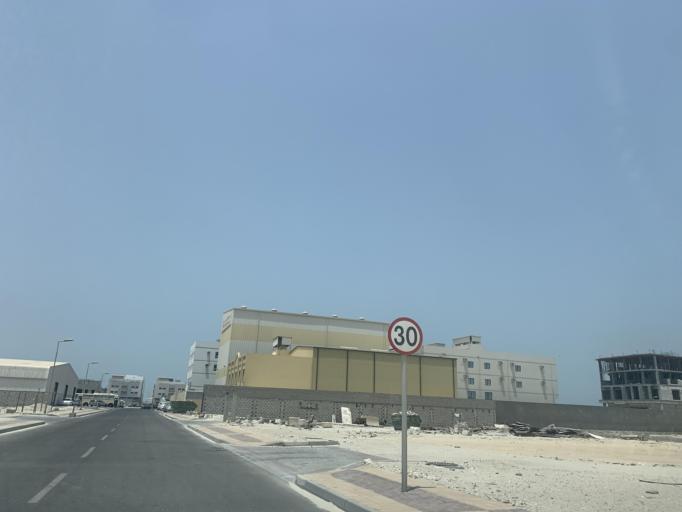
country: BH
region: Muharraq
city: Al Hadd
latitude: 26.2566
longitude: 50.6701
